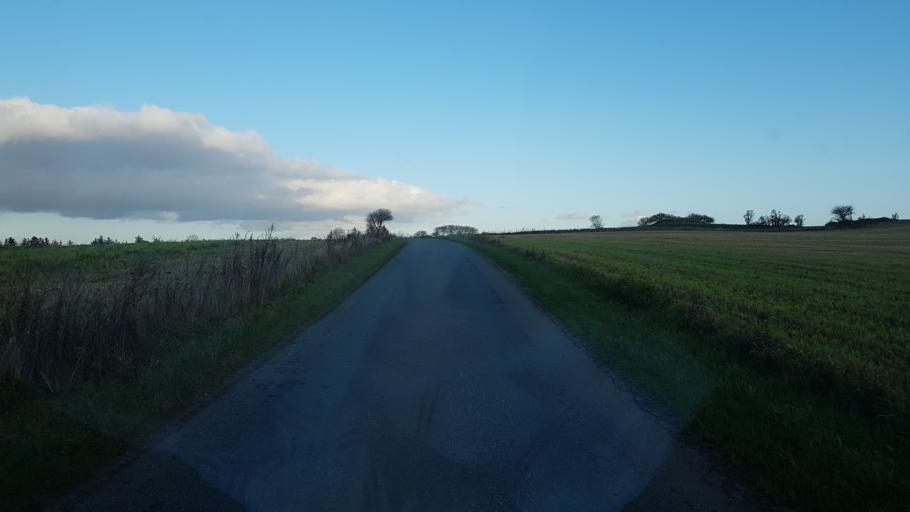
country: DK
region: South Denmark
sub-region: Vejen Kommune
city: Brorup
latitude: 55.4548
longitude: 8.9653
